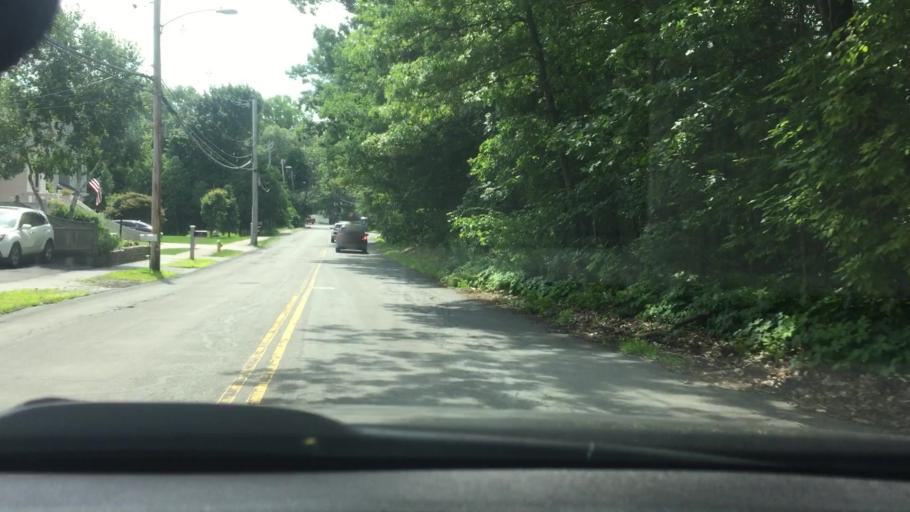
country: US
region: Massachusetts
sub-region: Norfolk County
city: Needham
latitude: 42.3081
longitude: -71.2397
